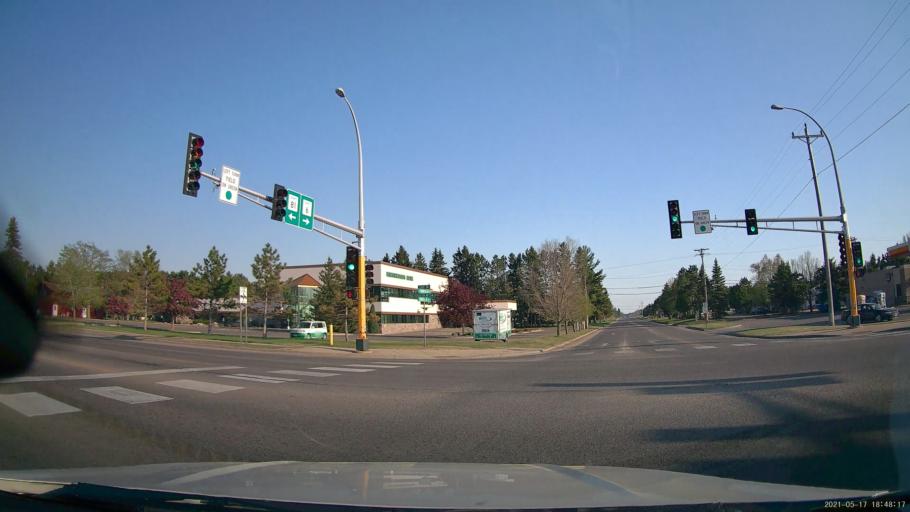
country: US
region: Minnesota
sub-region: Hubbard County
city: Park Rapids
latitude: 46.9219
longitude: -95.0369
